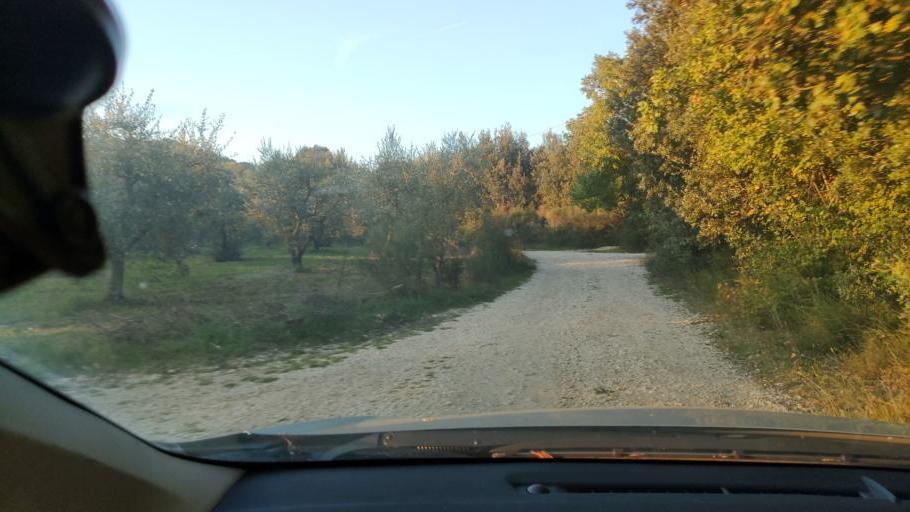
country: IT
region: Umbria
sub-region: Provincia di Terni
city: Amelia
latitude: 42.5809
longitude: 12.4348
